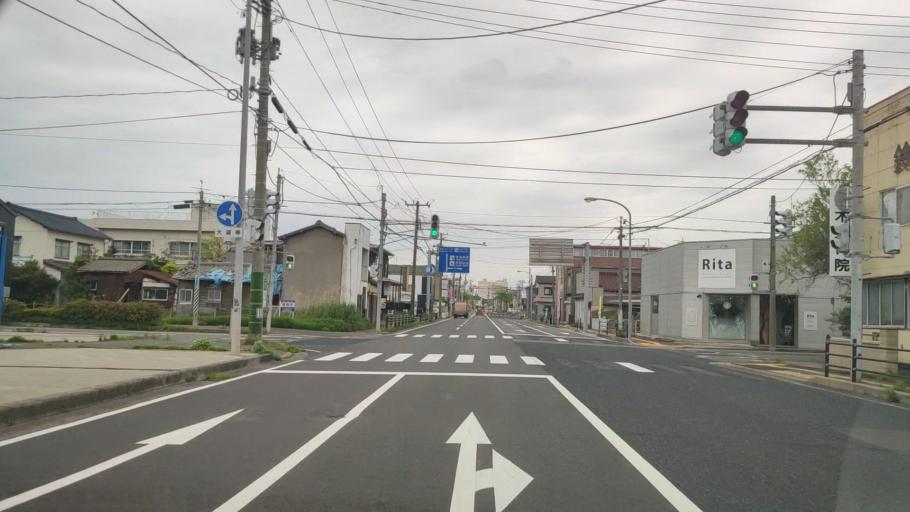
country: JP
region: Niigata
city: Niigata-shi
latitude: 37.9360
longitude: 139.0723
